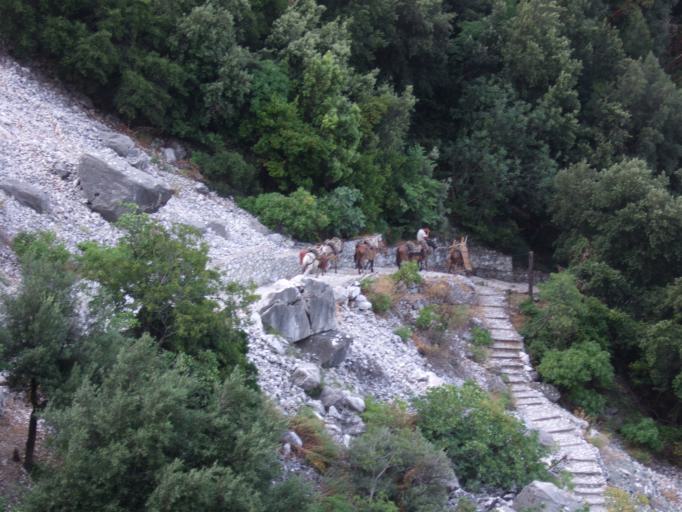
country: GR
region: Mount Athos
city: Karyes
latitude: 40.1396
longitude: 24.2973
